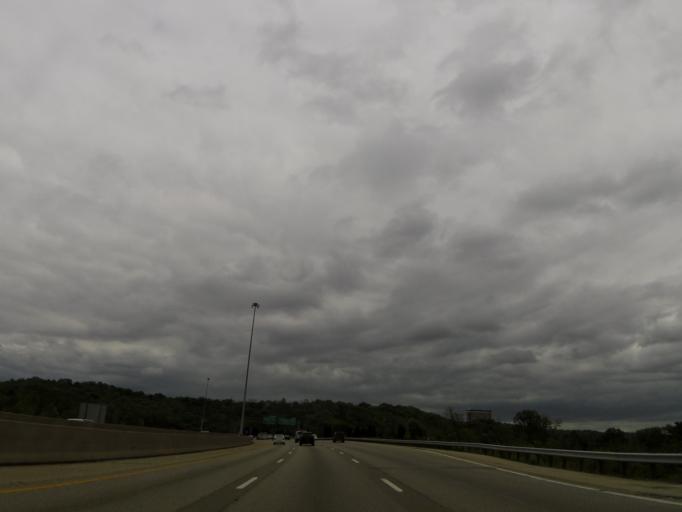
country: US
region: Ohio
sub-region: Hamilton County
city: Silverton
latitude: 39.1708
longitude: -84.4052
